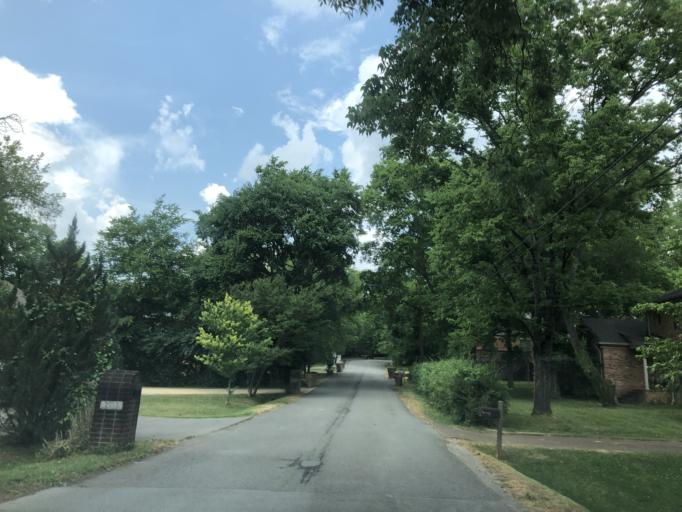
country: US
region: Tennessee
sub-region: Davidson County
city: Oak Hill
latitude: 36.1230
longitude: -86.8149
